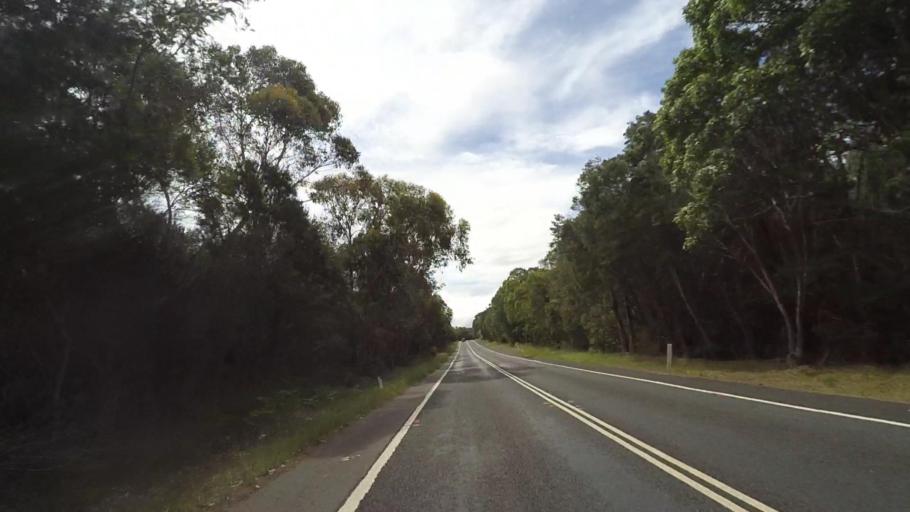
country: AU
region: New South Wales
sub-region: Sutherland Shire
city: Loftus
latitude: -34.0573
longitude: 151.0498
